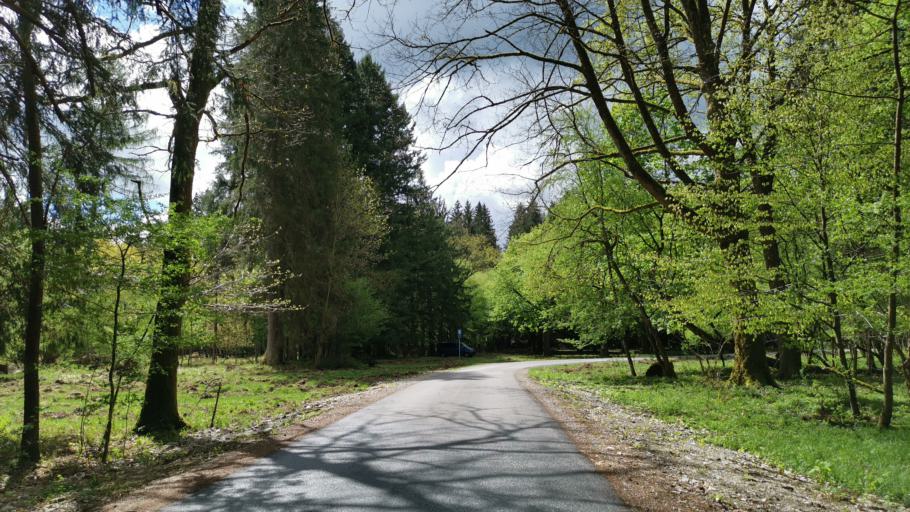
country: DE
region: Bavaria
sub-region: Upper Bavaria
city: Pullach im Isartal
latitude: 48.0601
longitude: 11.4896
